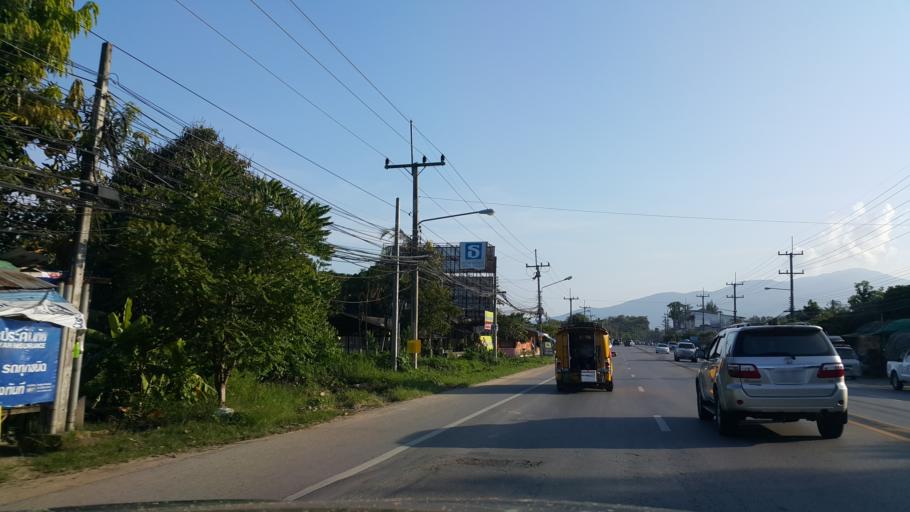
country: TH
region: Chiang Mai
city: San Sai
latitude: 18.9514
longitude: 98.9445
